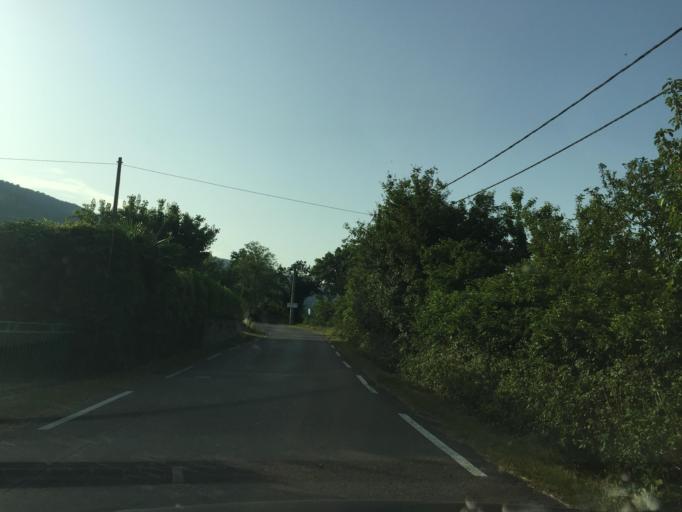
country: IT
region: Friuli Venezia Giulia
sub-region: Provincia di Trieste
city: Dolina
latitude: 45.5763
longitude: 13.8479
